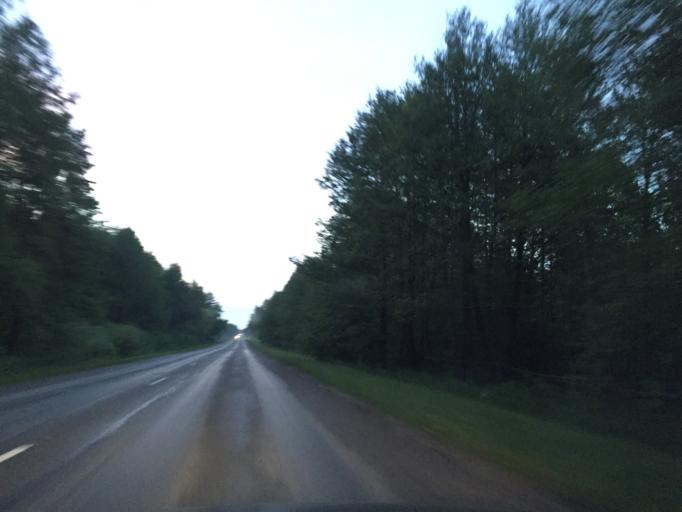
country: LT
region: Klaipedos apskritis
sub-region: Klaipeda
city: Palanga
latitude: 55.8928
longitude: 21.0642
